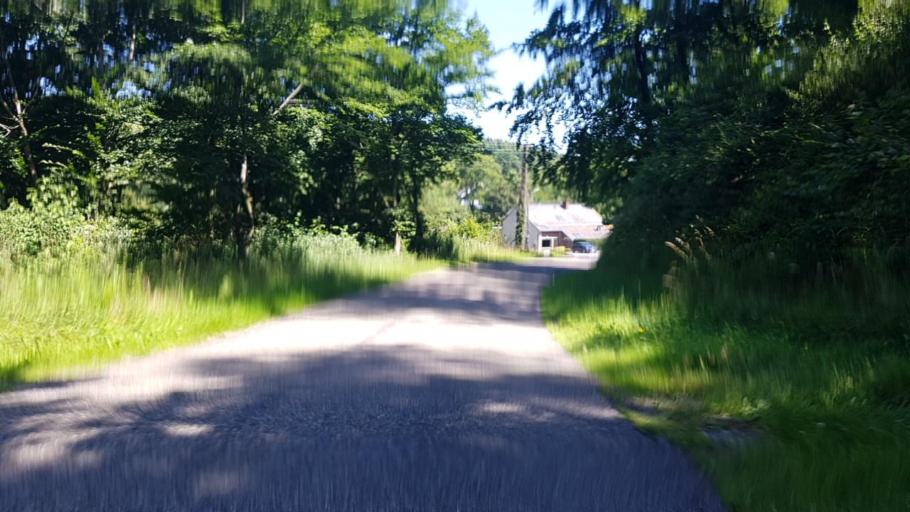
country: BE
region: Wallonia
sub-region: Province du Hainaut
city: Froidchapelle
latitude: 50.1260
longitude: 4.2473
